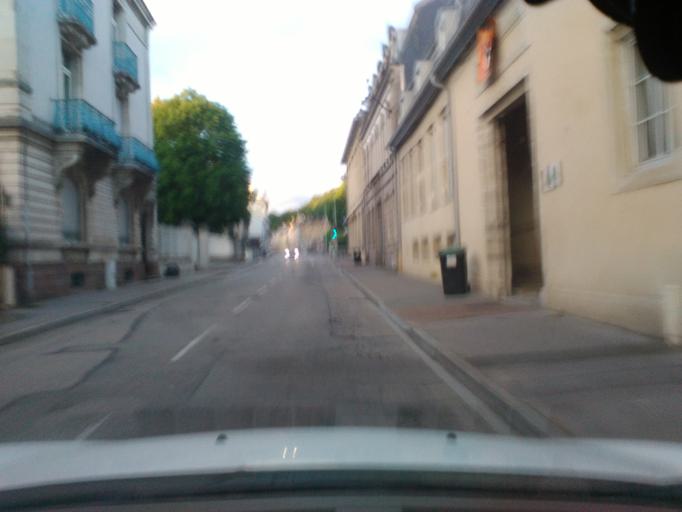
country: FR
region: Lorraine
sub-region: Departement des Vosges
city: Epinal
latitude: 48.1729
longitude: 6.4501
